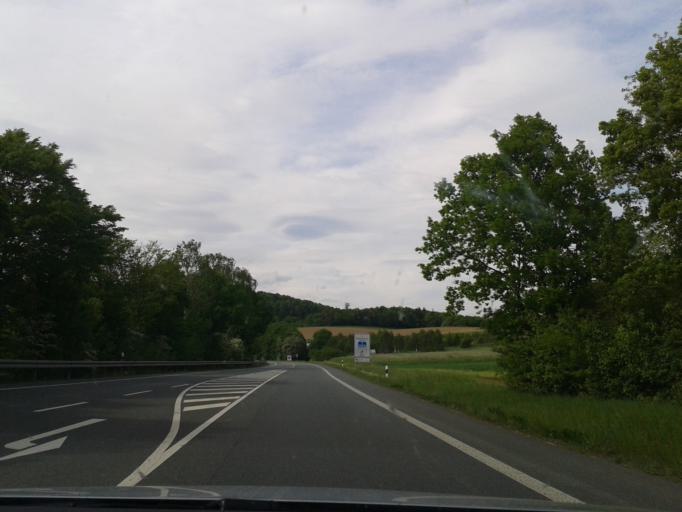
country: DE
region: Hesse
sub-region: Regierungsbezirk Kassel
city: Vohl
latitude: 51.1712
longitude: 8.8933
